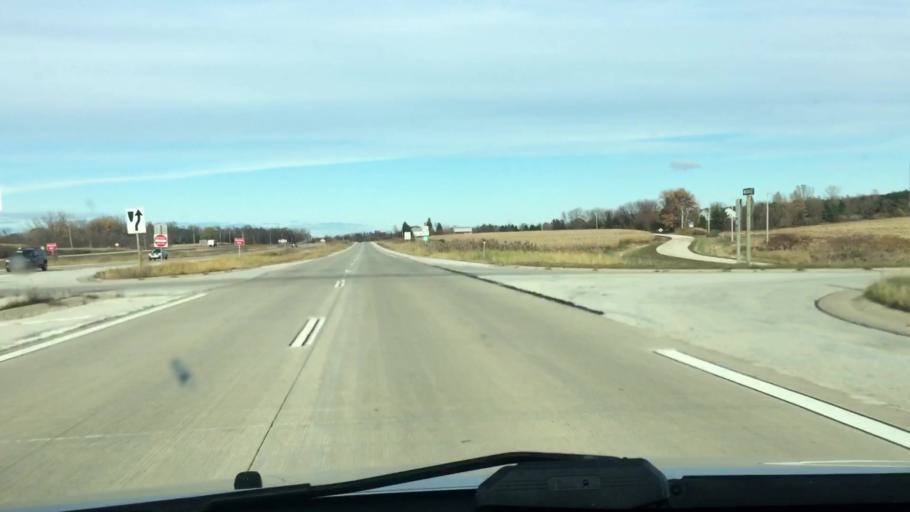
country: US
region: Wisconsin
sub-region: Kewaunee County
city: Luxemburg
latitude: 44.6587
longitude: -87.7467
